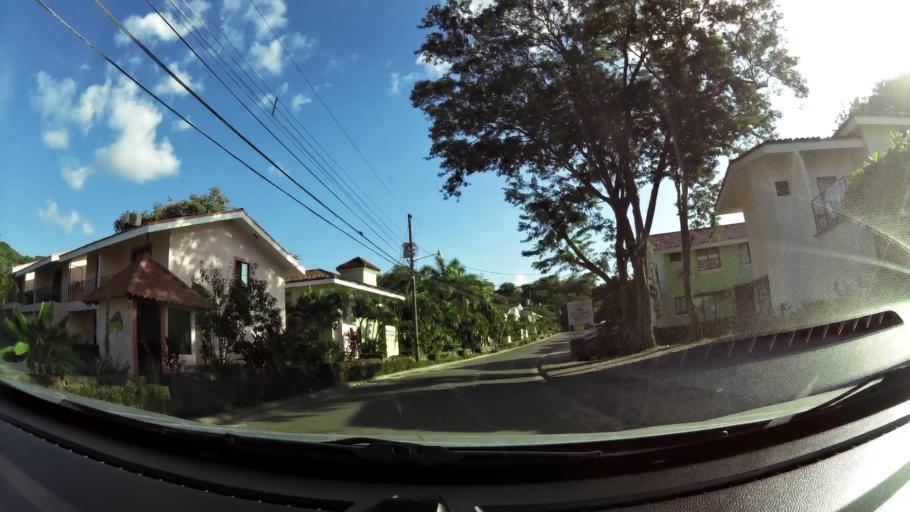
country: CR
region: Guanacaste
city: Sardinal
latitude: 10.5530
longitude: -85.6907
